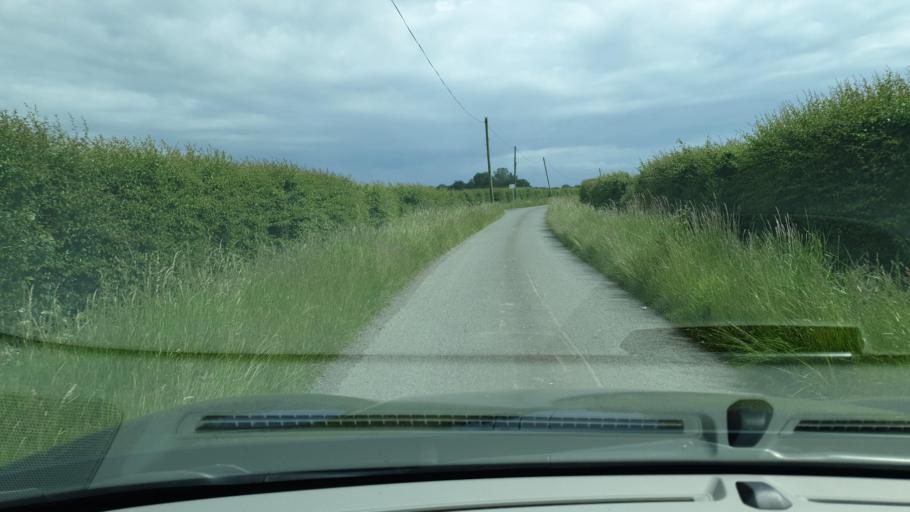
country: IE
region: Leinster
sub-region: An Mhi
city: Ratoath
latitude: 53.4567
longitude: -6.4559
